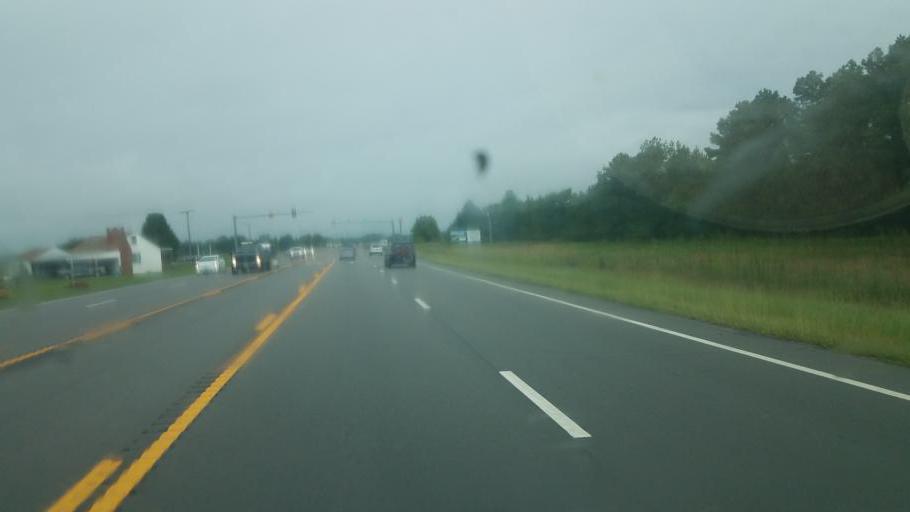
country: US
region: North Carolina
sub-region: Currituck County
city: Moyock
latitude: 36.5085
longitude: -76.1583
